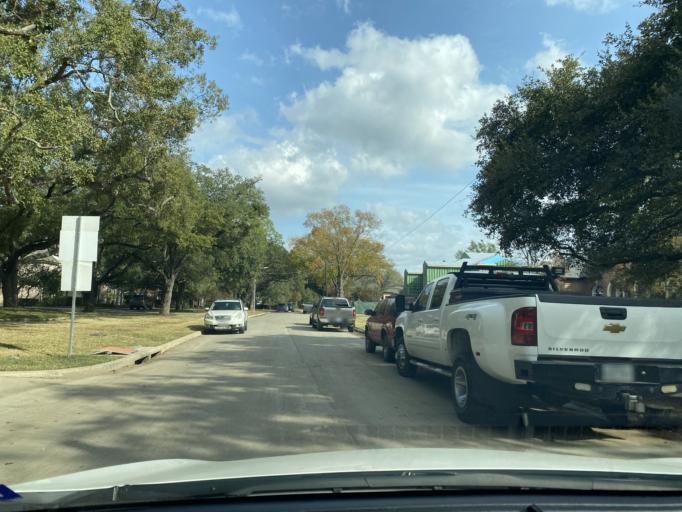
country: US
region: Texas
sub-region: Harris County
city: Hunters Creek Village
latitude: 29.7601
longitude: -95.4706
